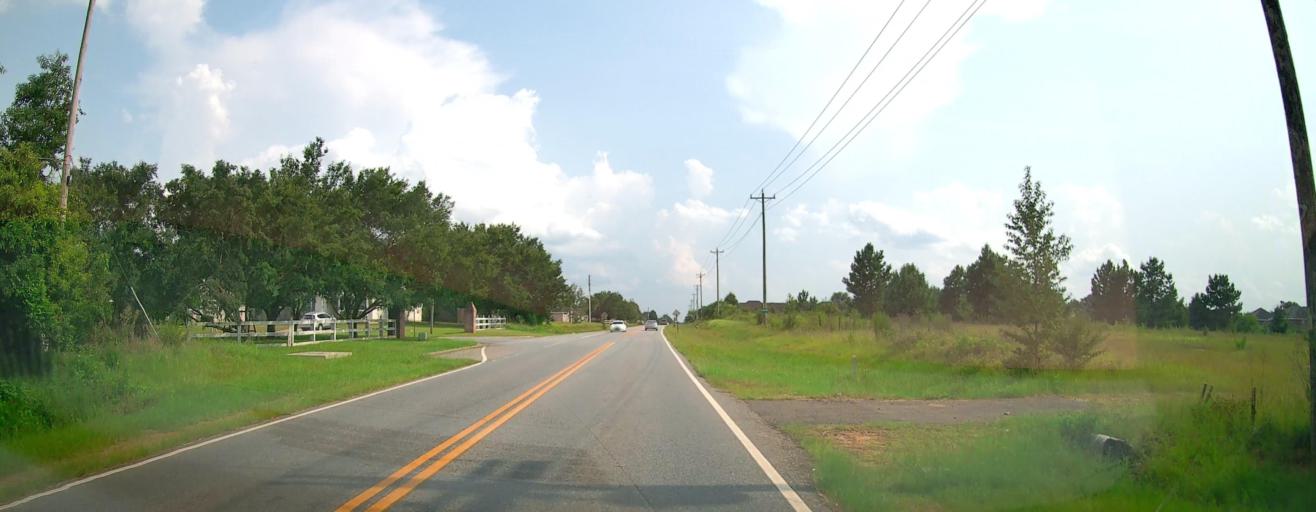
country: US
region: Georgia
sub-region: Houston County
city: Centerville
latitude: 32.5710
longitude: -83.6525
